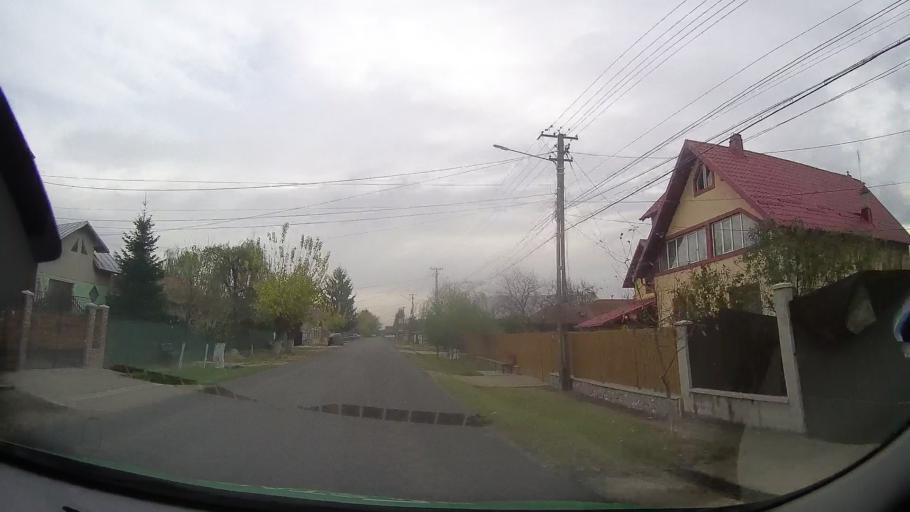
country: RO
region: Prahova
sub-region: Comuna Valea Calugareasca
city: Pantazi
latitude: 44.9372
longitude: 26.1374
